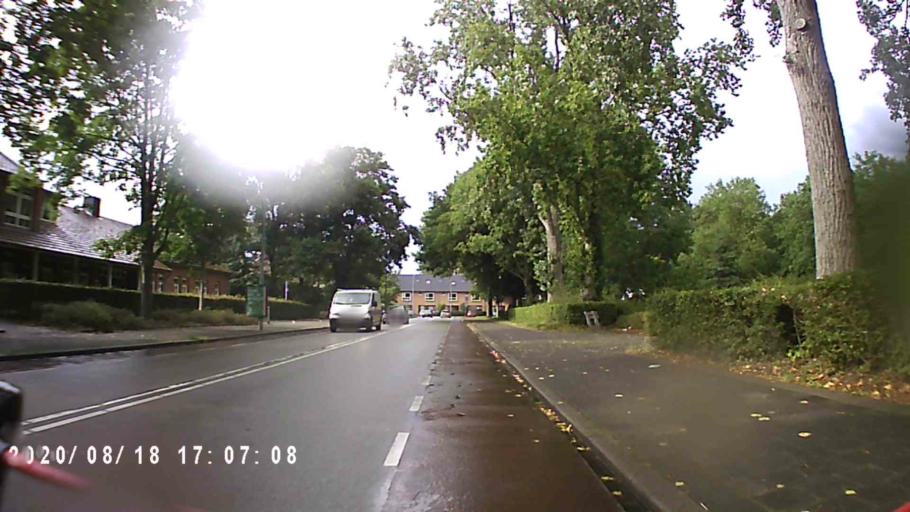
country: NL
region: Groningen
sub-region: Gemeente Groningen
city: Groningen
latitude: 53.2283
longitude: 6.5252
